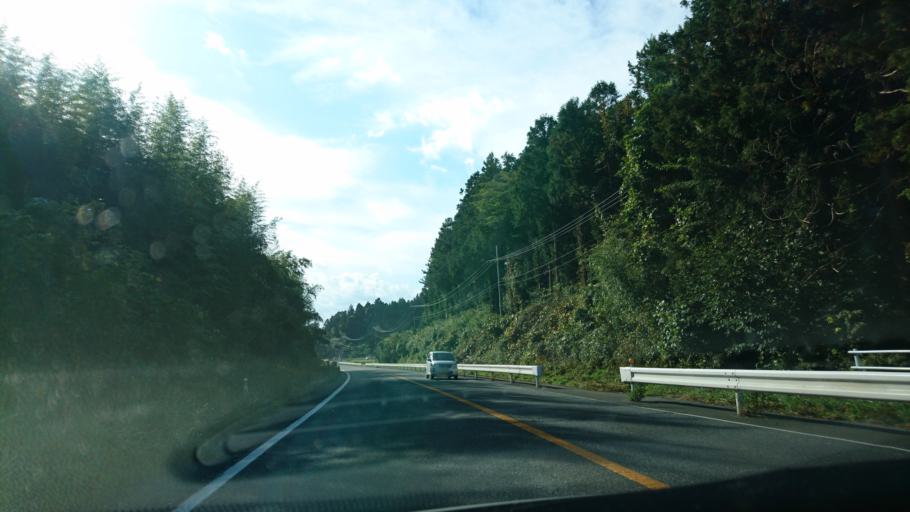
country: JP
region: Miyagi
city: Furukawa
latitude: 38.6265
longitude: 140.9823
